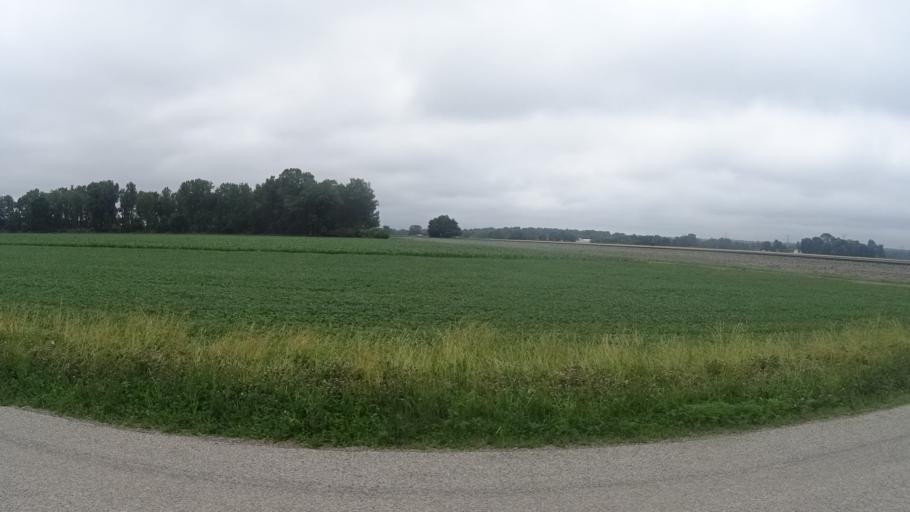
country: US
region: Ohio
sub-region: Erie County
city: Huron
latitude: 41.3415
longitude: -82.5439
